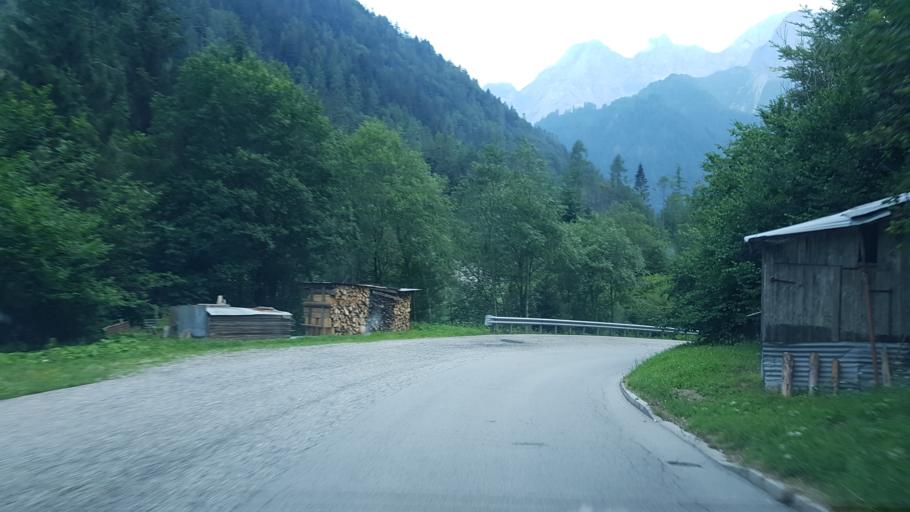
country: IT
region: Friuli Venezia Giulia
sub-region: Provincia di Udine
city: Forni Avoltri
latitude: 46.5966
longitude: 12.7767
